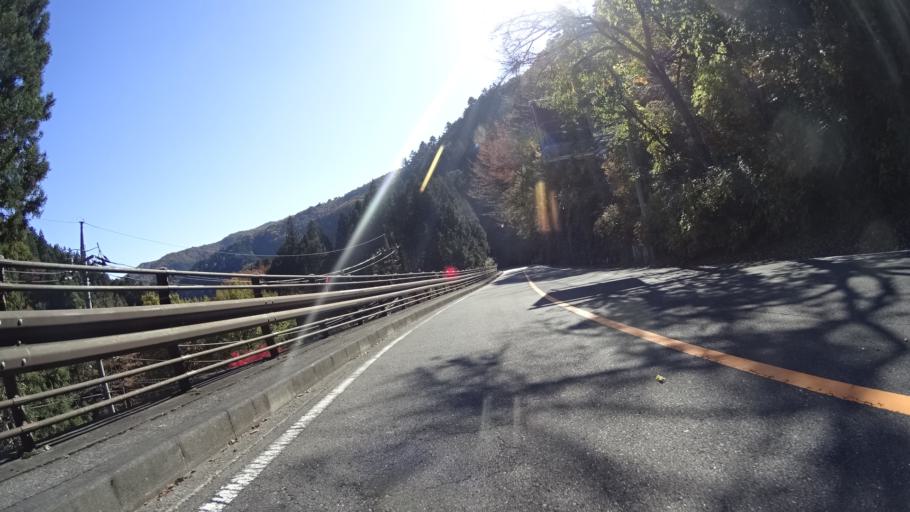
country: JP
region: Yamanashi
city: Uenohara
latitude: 35.7318
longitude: 139.0402
